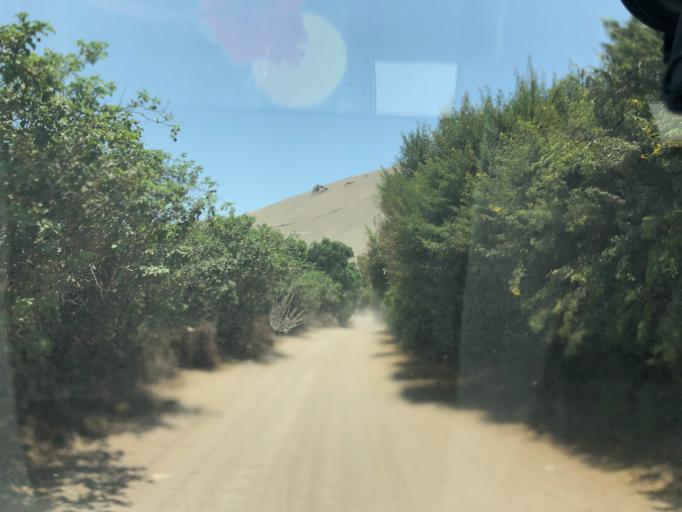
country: PE
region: Lima
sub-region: Provincia de Canete
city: San Vicente de Canete
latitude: -13.0104
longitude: -76.4639
